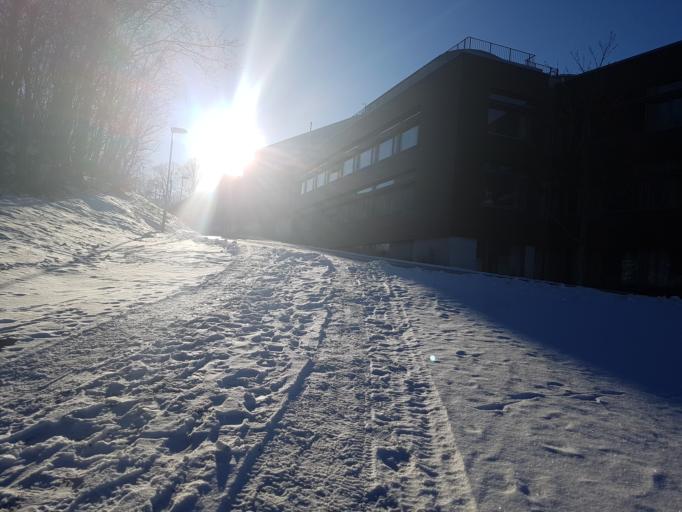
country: NO
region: Sor-Trondelag
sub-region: Trondheim
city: Trondheim
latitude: 63.4547
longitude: 10.4539
